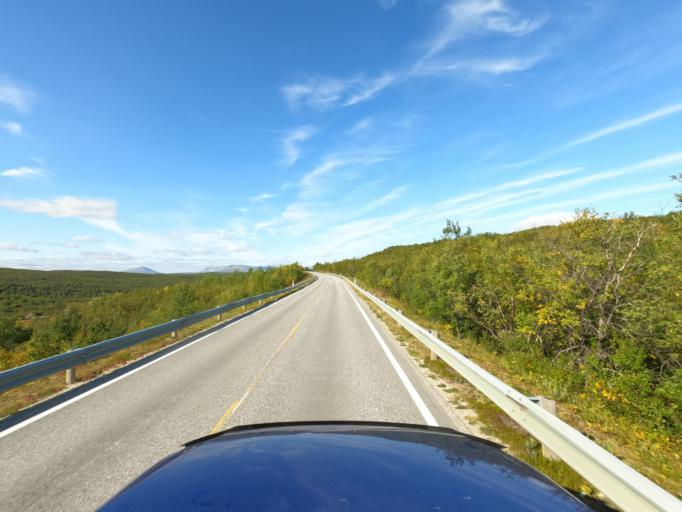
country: NO
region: Finnmark Fylke
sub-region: Porsanger
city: Lakselv
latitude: 69.7662
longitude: 25.1766
